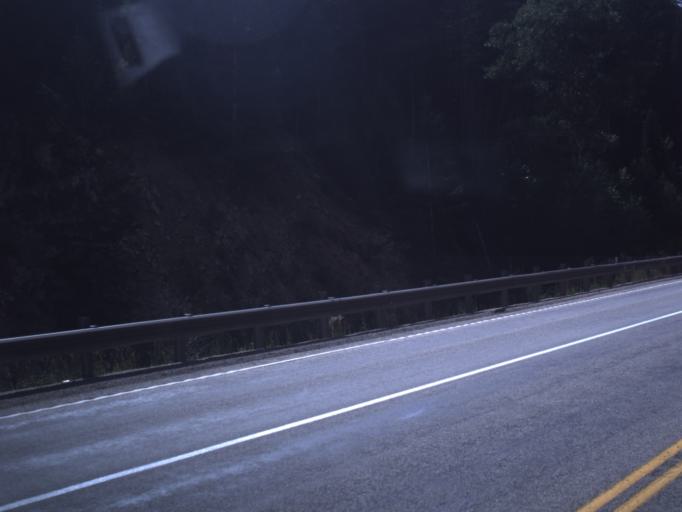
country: US
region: Utah
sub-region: Wasatch County
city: Heber
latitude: 40.3548
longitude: -111.2786
